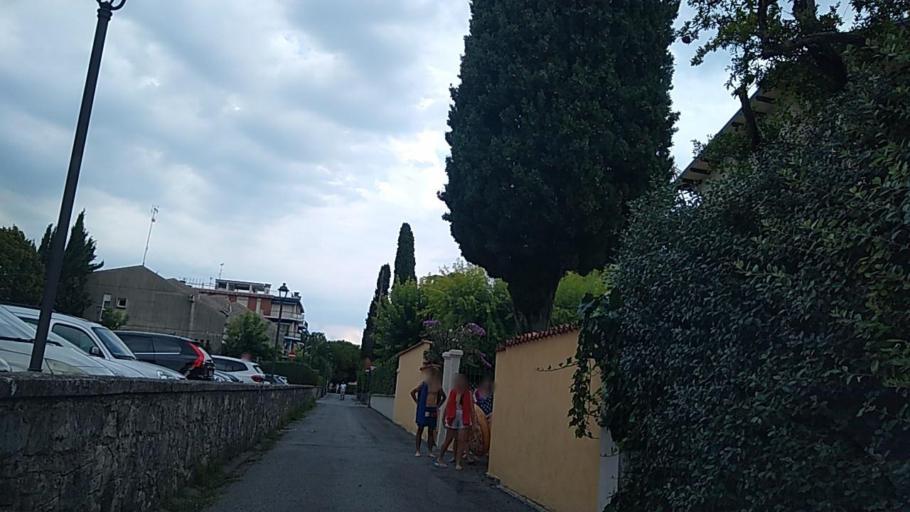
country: IT
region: Lombardy
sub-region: Provincia di Brescia
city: Gardone Riviera
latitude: 45.6134
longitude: 10.5508
